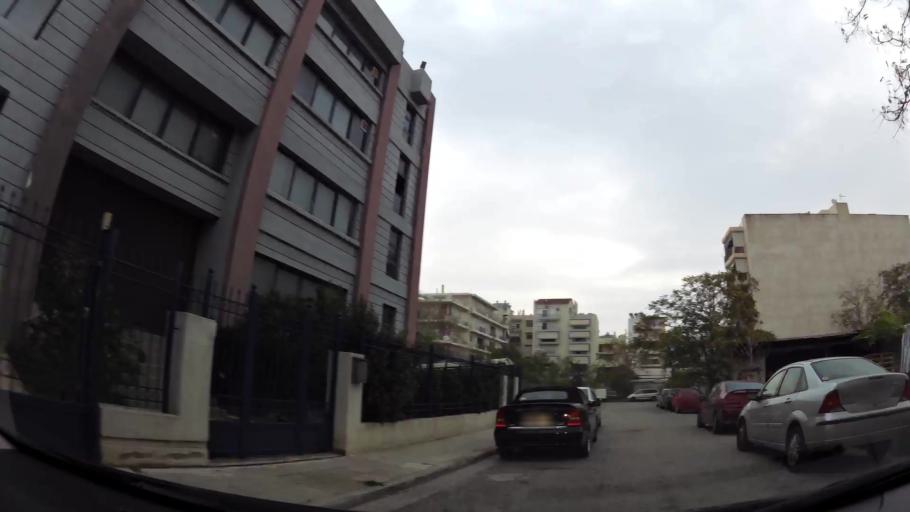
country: GR
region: Attica
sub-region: Nomarchia Athinas
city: Athens
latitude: 37.9770
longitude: 23.7042
